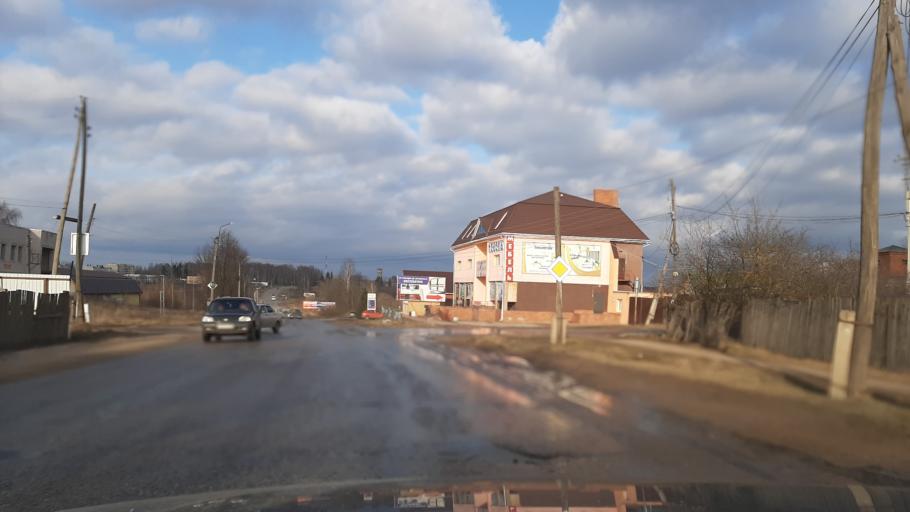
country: RU
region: Ivanovo
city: Teykovo
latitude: 56.8638
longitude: 40.5639
